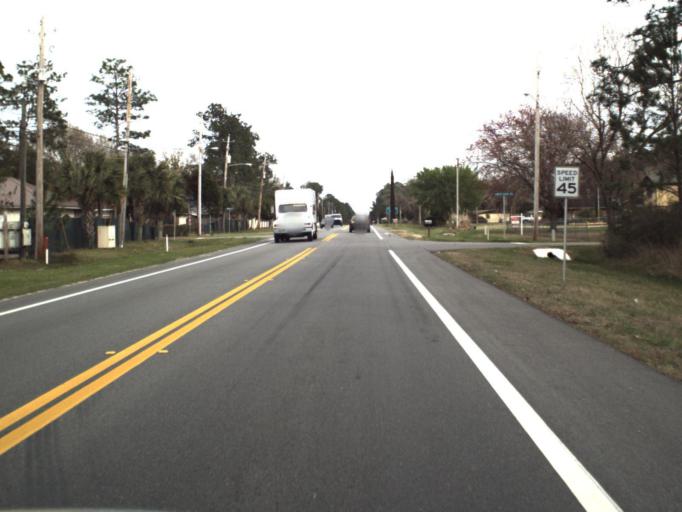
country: US
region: Florida
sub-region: Bay County
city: Callaway
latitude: 30.1528
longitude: -85.5493
